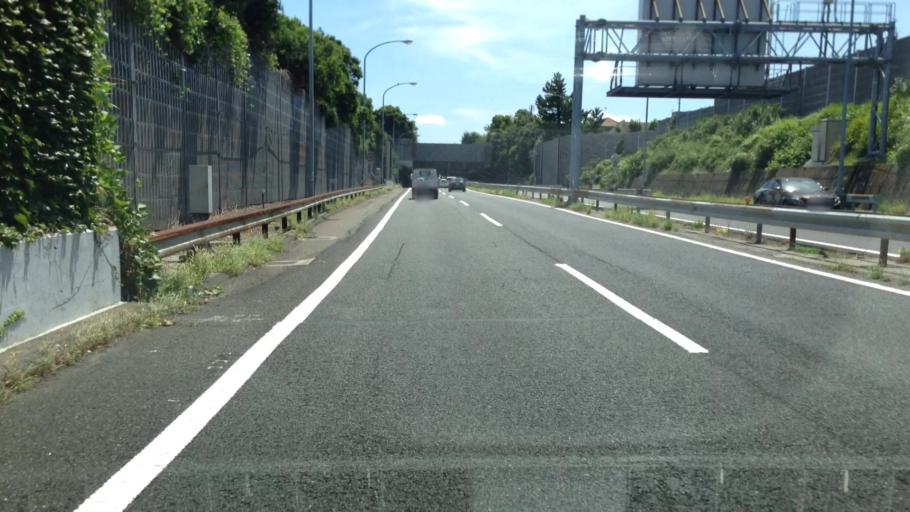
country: JP
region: Kanagawa
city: Yokohama
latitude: 35.4065
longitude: 139.5751
